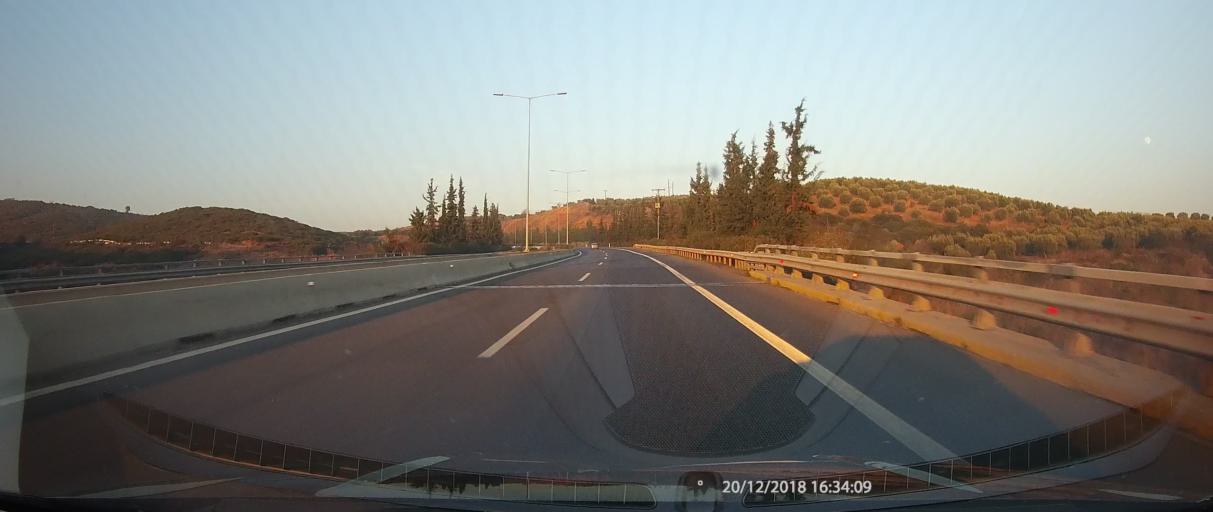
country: GR
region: Thessaly
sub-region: Nomos Magnisias
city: Nea Anchialos
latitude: 39.2772
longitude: 22.7435
